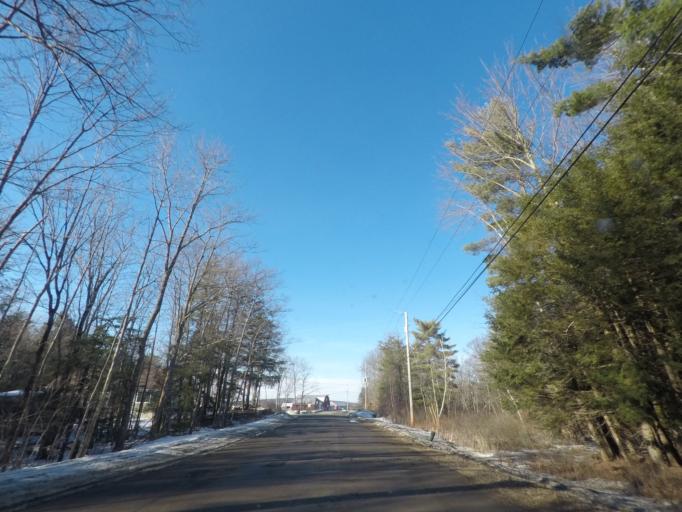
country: US
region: New York
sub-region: Rensselaer County
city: Averill Park
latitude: 42.6398
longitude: -73.5239
